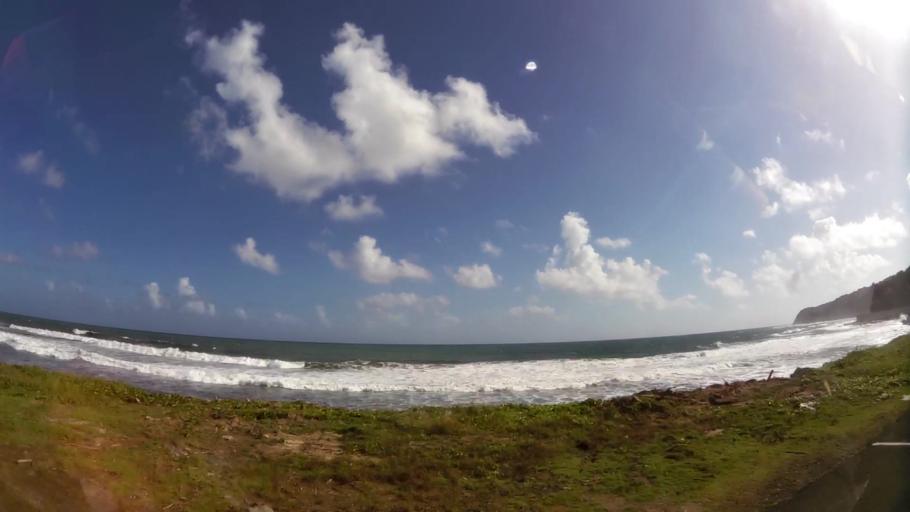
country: DM
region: Saint Andrew
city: Marigot
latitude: 15.5459
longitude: -61.2914
